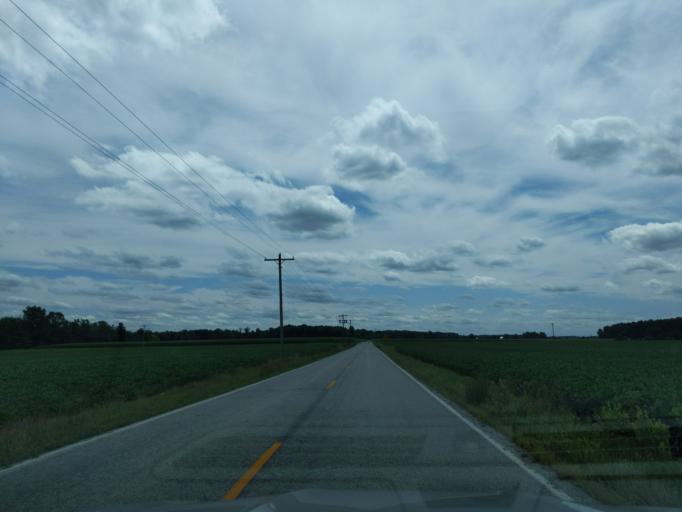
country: US
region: Indiana
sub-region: Ripley County
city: Batesville
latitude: 39.2302
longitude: -85.2679
